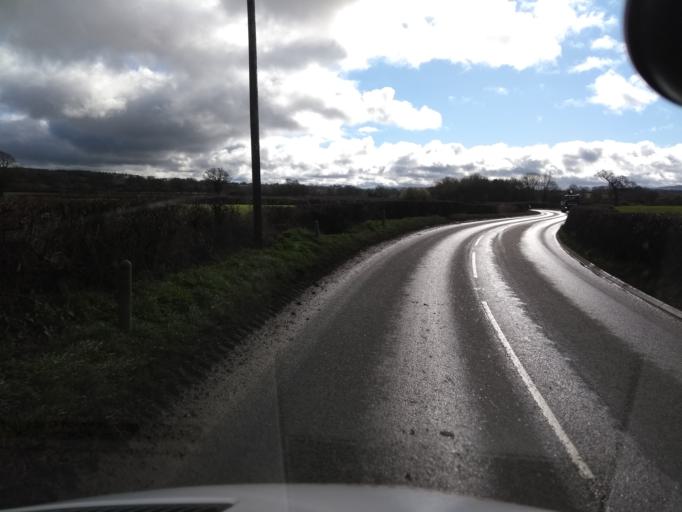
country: GB
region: England
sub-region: Somerset
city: Milborne Port
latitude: 50.9234
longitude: -2.4725
